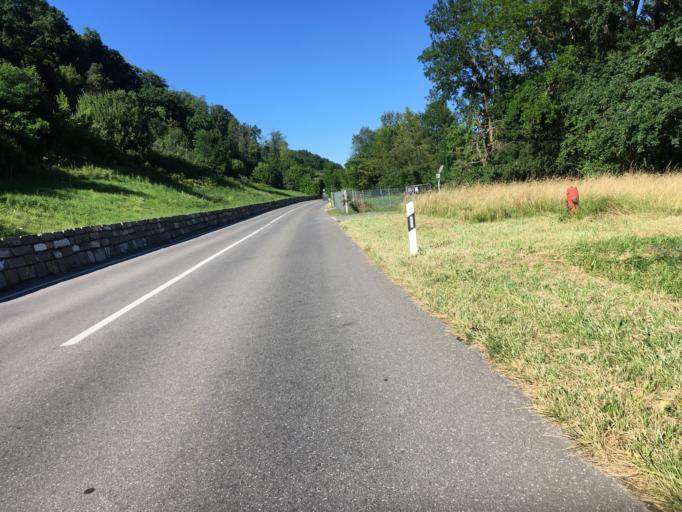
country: CH
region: Vaud
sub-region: Broye-Vully District
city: Avenches
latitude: 46.9335
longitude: 7.0478
